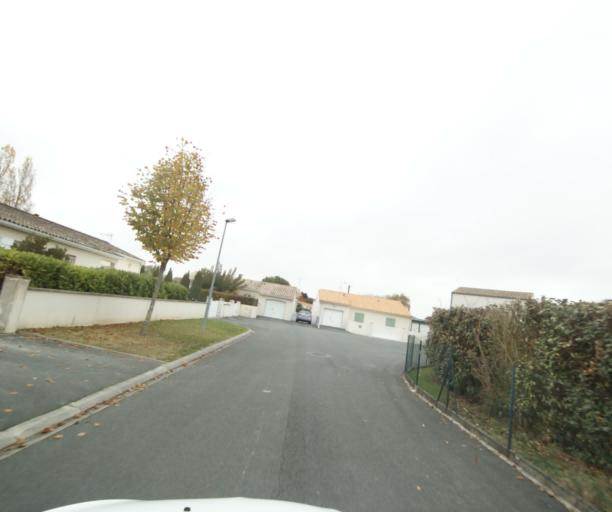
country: FR
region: Poitou-Charentes
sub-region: Departement de la Charente-Maritime
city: Les Gonds
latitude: 45.7335
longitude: -0.6193
